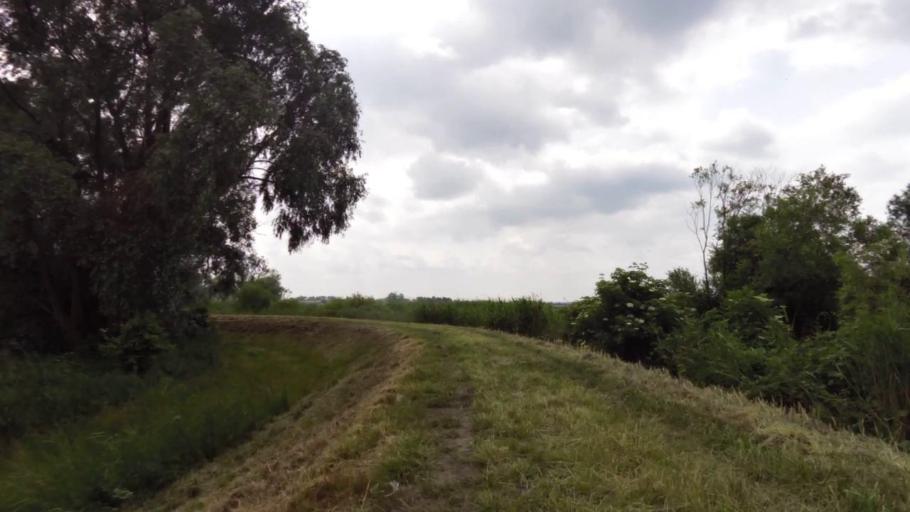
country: PL
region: West Pomeranian Voivodeship
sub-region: Powiat policki
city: Police
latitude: 53.5094
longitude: 14.6955
